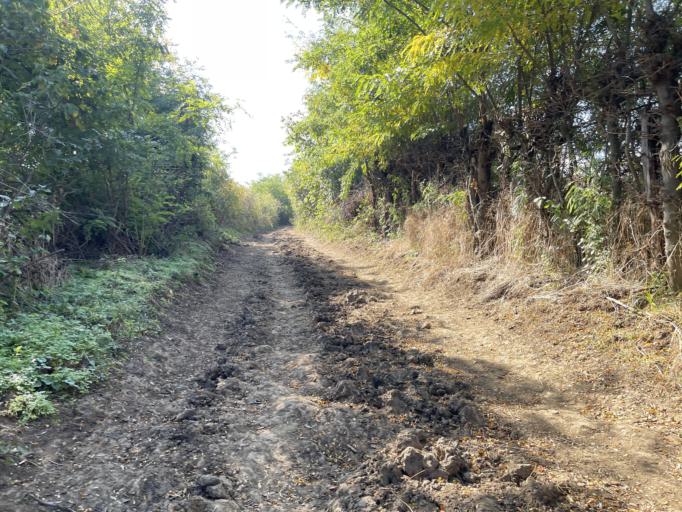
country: RO
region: Iasi
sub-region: Comuna Dumesti
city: Pausesti
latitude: 47.1566
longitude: 27.3137
